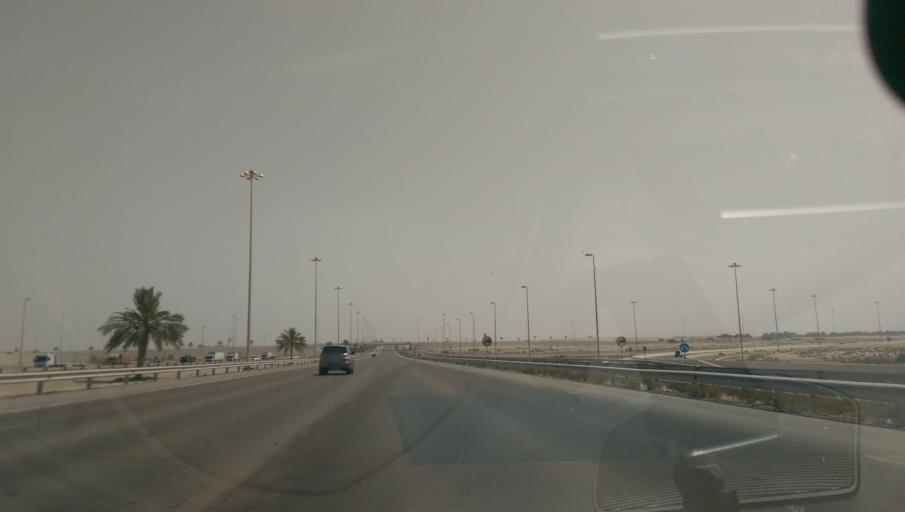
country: AE
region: Abu Dhabi
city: Abu Dhabi
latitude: 24.4028
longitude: 54.6701
